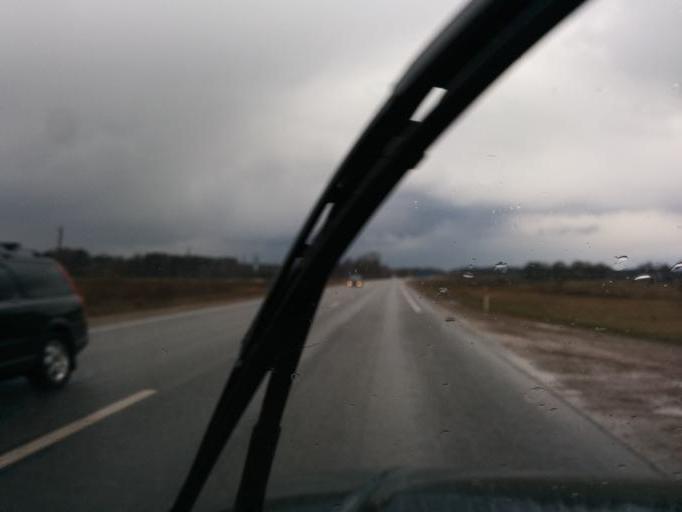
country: LV
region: Babite
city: Pinki
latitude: 56.8714
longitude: 23.9631
